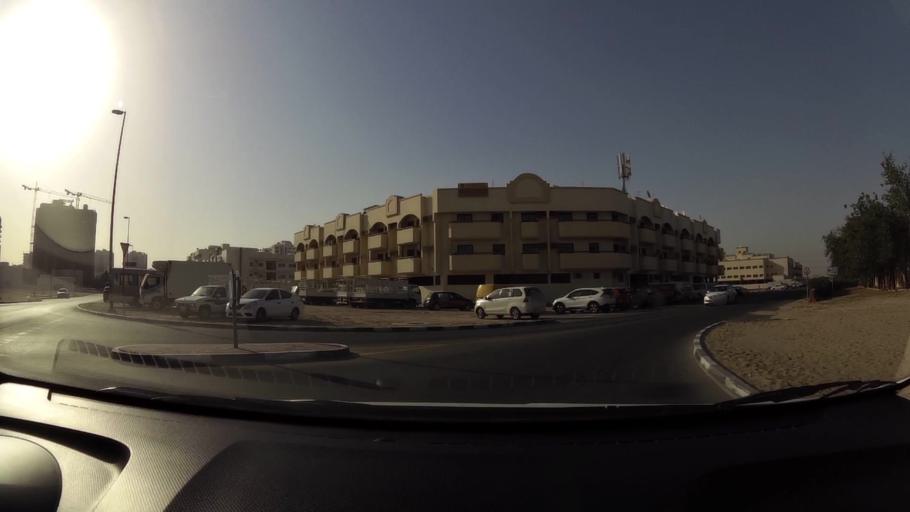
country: AE
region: Ash Shariqah
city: Sharjah
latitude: 25.2714
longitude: 55.3837
